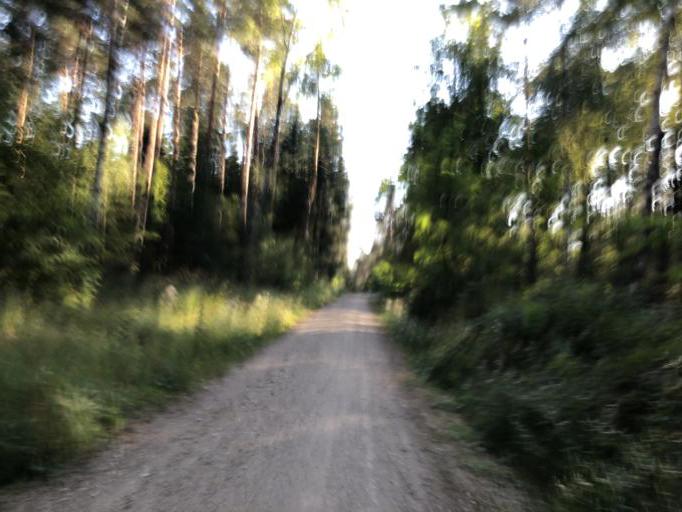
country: DE
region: Bavaria
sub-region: Regierungsbezirk Mittelfranken
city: Uttenreuth
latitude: 49.5582
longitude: 11.0805
